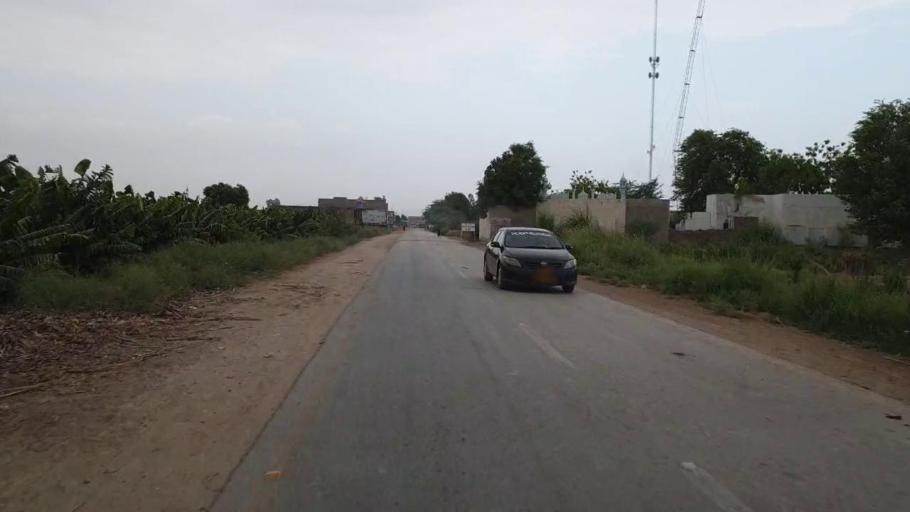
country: PK
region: Sindh
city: Bandhi
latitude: 26.5899
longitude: 68.2963
